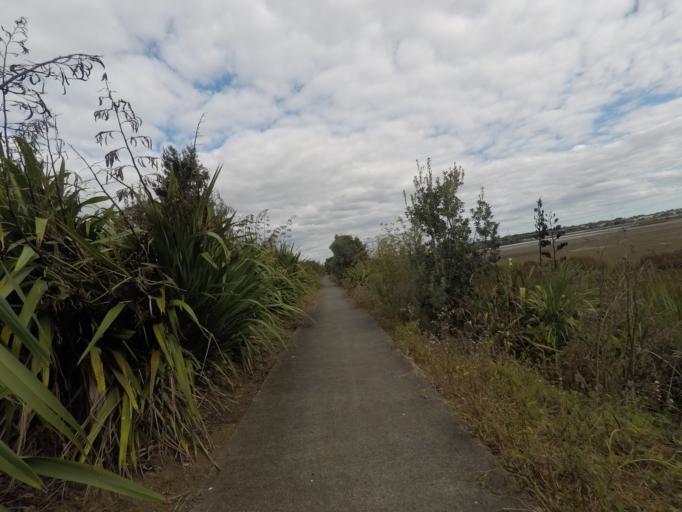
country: NZ
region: Auckland
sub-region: Auckland
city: Papakura
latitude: -37.0529
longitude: 174.9266
